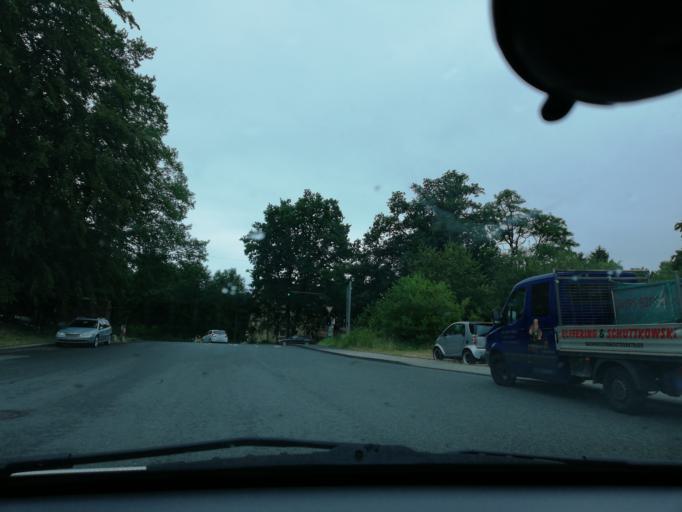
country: DE
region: North Rhine-Westphalia
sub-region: Regierungsbezirk Dusseldorf
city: Wuppertal
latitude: 51.2381
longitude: 7.1998
